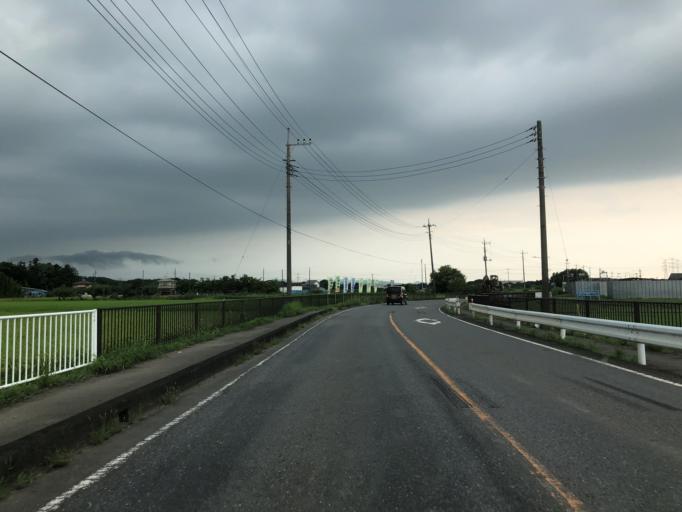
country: JP
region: Saitama
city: Sakado
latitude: 36.0189
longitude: 139.4016
